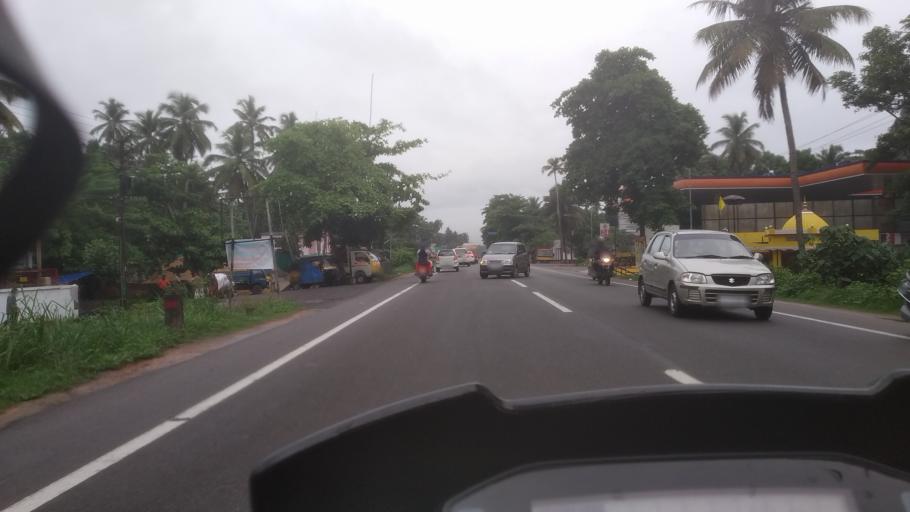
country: IN
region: Kerala
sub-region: Alappuzha
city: Kayankulam
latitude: 9.1641
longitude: 76.5031
